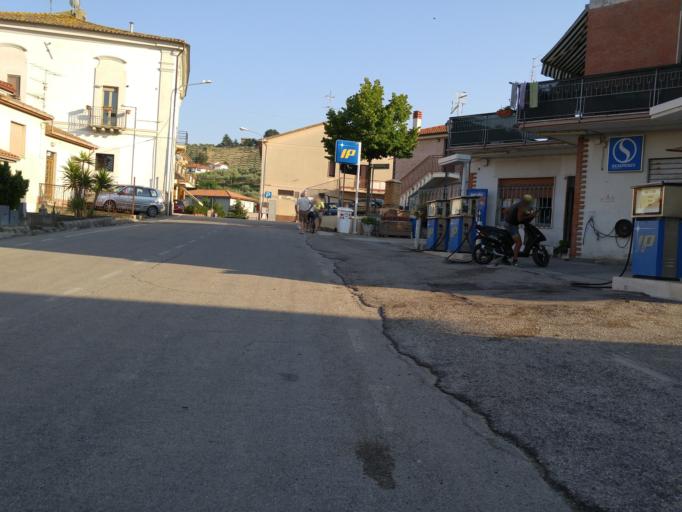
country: IT
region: Abruzzo
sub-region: Provincia di Teramo
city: Castilenti
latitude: 42.5597
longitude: 13.9221
